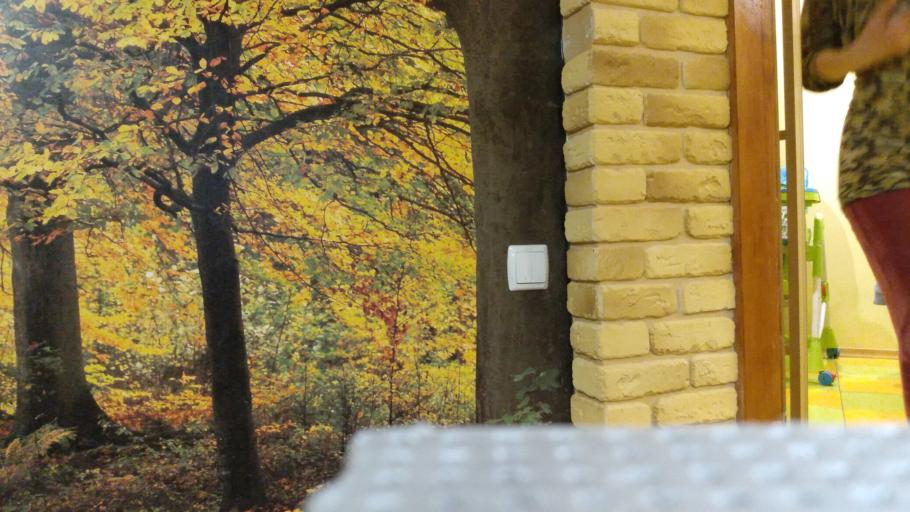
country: RU
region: Vologda
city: Babayevo
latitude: 59.3679
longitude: 35.9970
